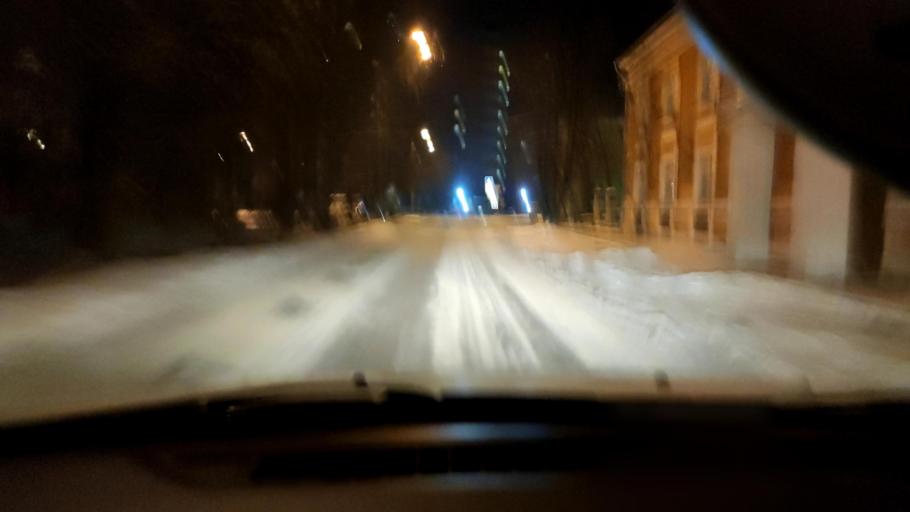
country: RU
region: Perm
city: Kultayevo
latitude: 58.0047
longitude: 55.9636
